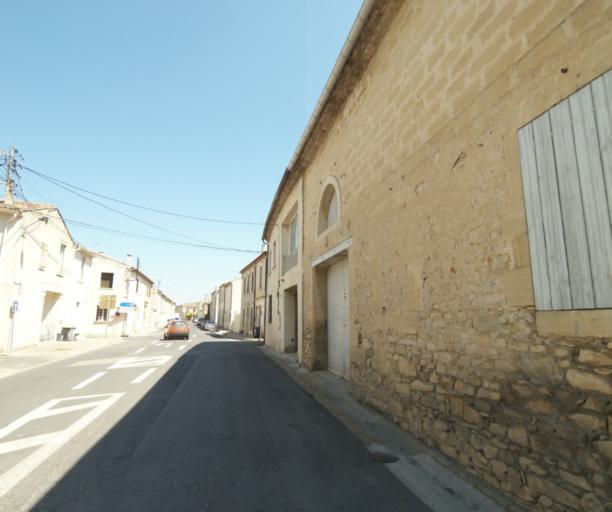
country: FR
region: Languedoc-Roussillon
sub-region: Departement de l'Herault
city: Marsillargues
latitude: 43.6670
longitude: 4.1779
